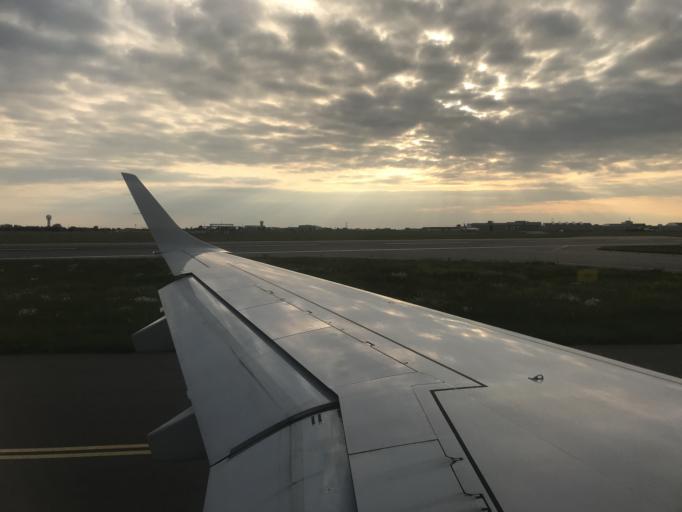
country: PL
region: Masovian Voivodeship
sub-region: Warszawa
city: Wlochy
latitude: 52.1725
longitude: 20.9675
